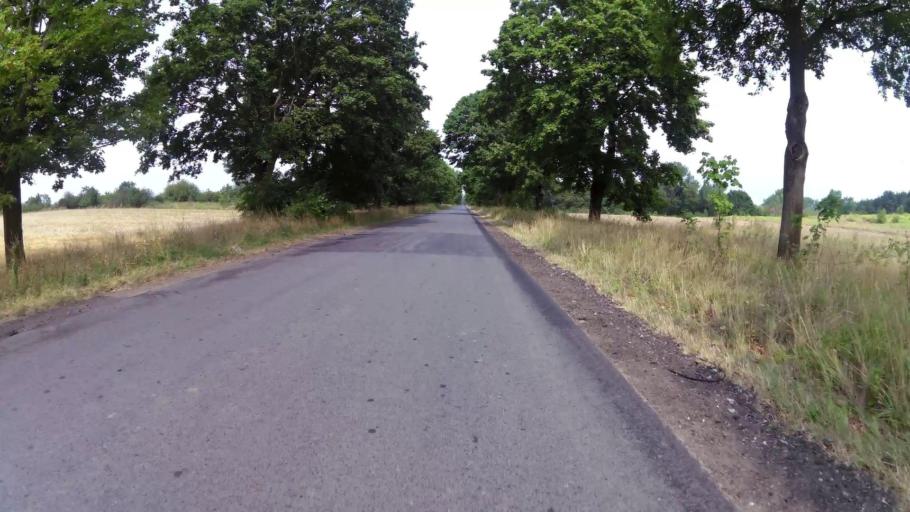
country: PL
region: West Pomeranian Voivodeship
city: Trzcinsko Zdroj
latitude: 52.9569
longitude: 14.6234
